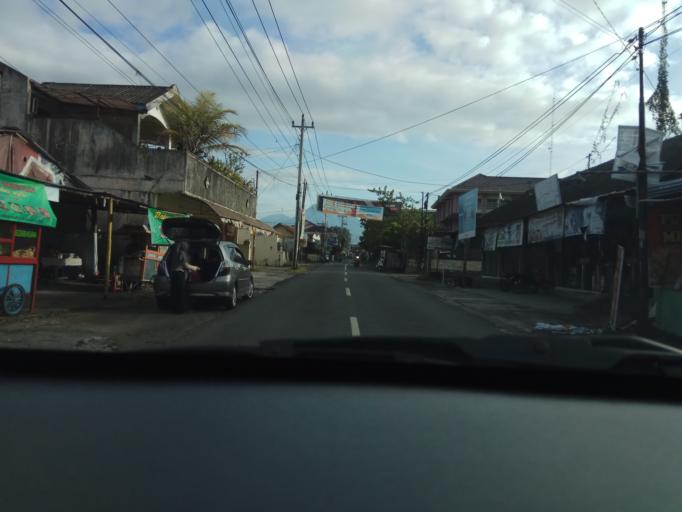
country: ID
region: Daerah Istimewa Yogyakarta
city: Depok
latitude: -7.7624
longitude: 110.4065
